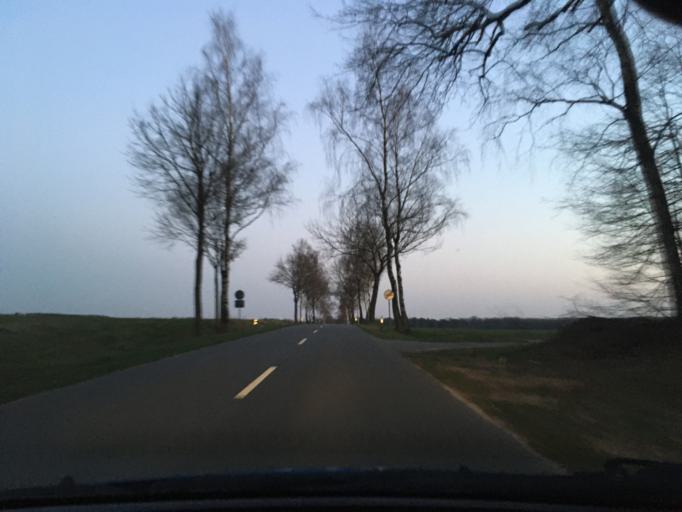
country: DE
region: Lower Saxony
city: Rehlingen
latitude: 53.0730
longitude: 10.2320
